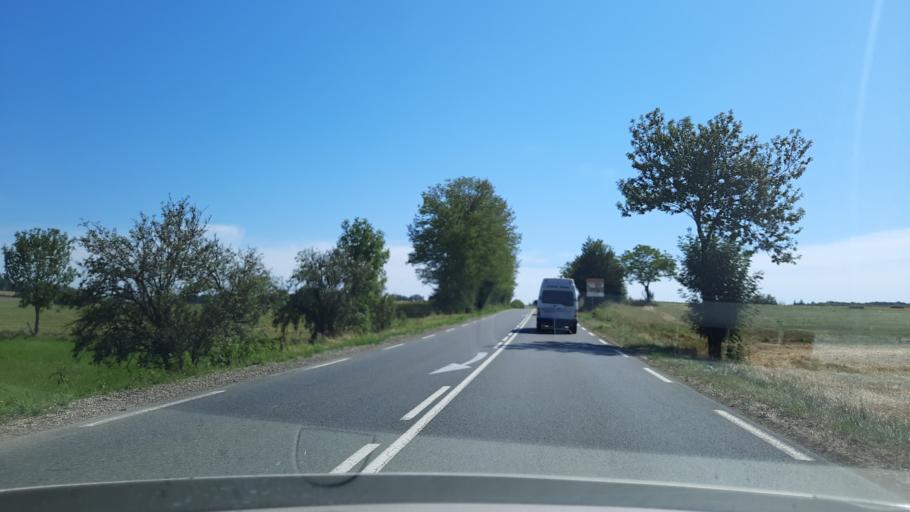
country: FR
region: Midi-Pyrenees
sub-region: Departement de l'Aveyron
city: Villefranche-de-Rouergue
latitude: 44.3471
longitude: 1.9613
